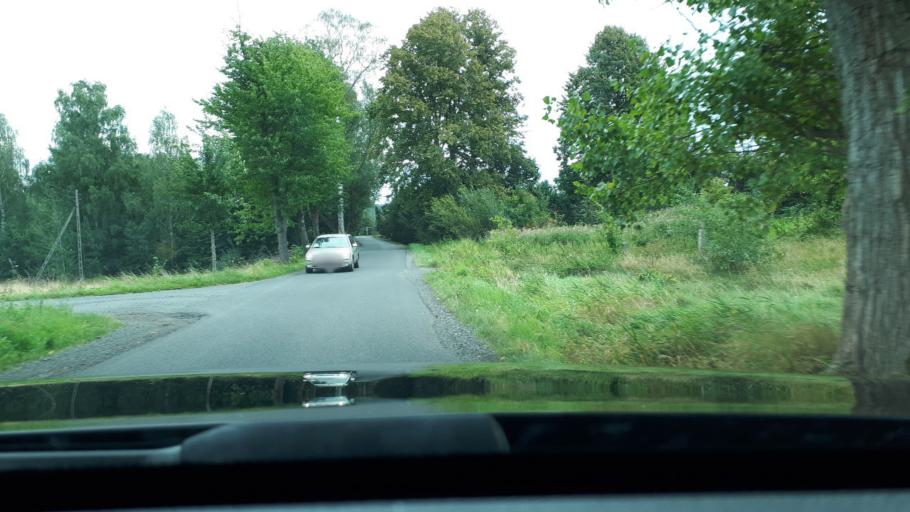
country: PL
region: Lower Silesian Voivodeship
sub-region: Powiat lubanski
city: Lesna
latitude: 51.0367
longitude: 15.3078
